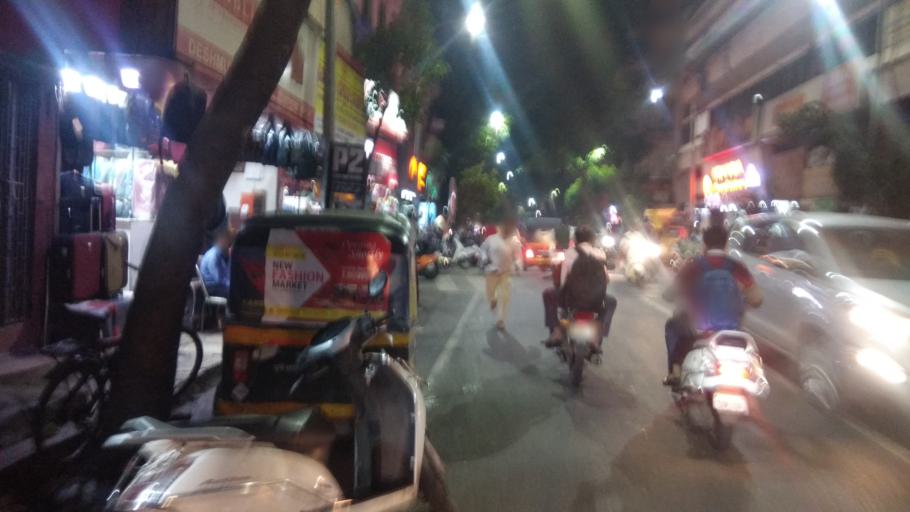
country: IN
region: Maharashtra
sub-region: Pune Division
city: Pune
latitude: 18.5188
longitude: 73.8584
